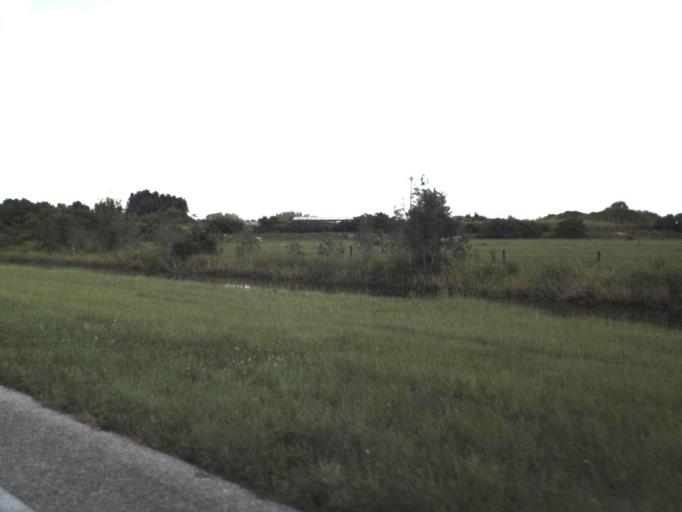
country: US
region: Florida
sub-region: Lee County
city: Suncoast Estates
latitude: 26.7830
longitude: -81.9395
